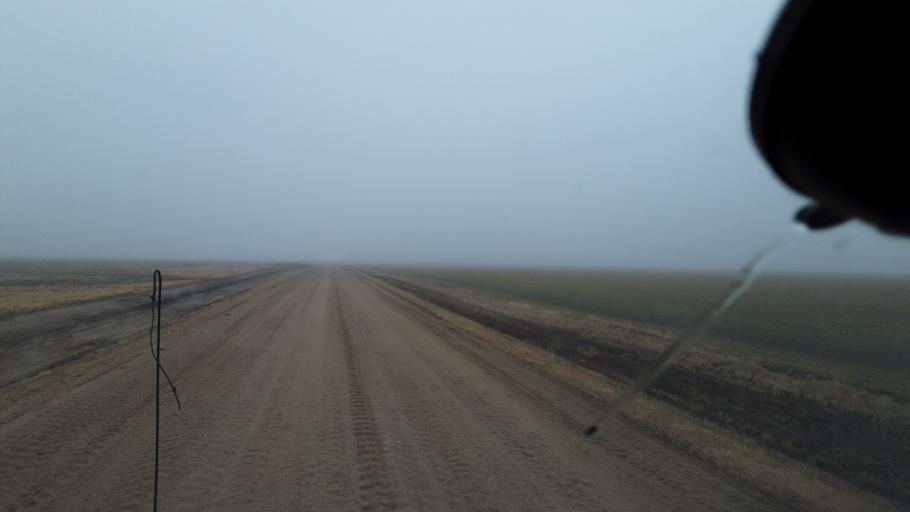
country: US
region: Kansas
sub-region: Reno County
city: South Hutchinson
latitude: 37.9842
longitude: -97.9788
